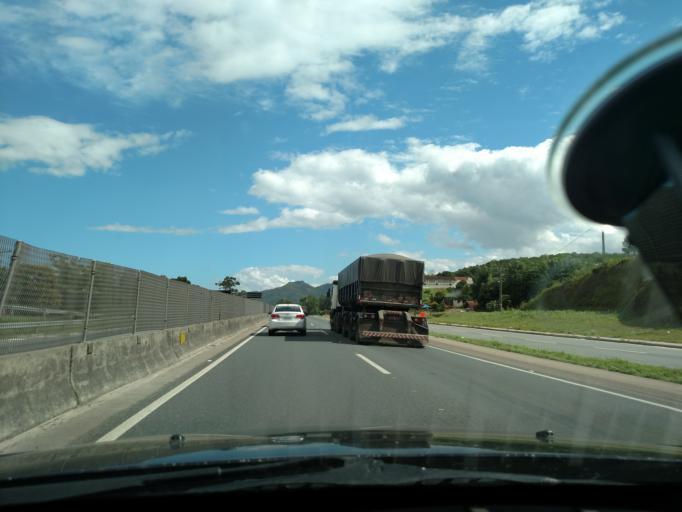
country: BR
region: Santa Catarina
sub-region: Biguacu
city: Biguacu
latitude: -27.3845
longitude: -48.6314
